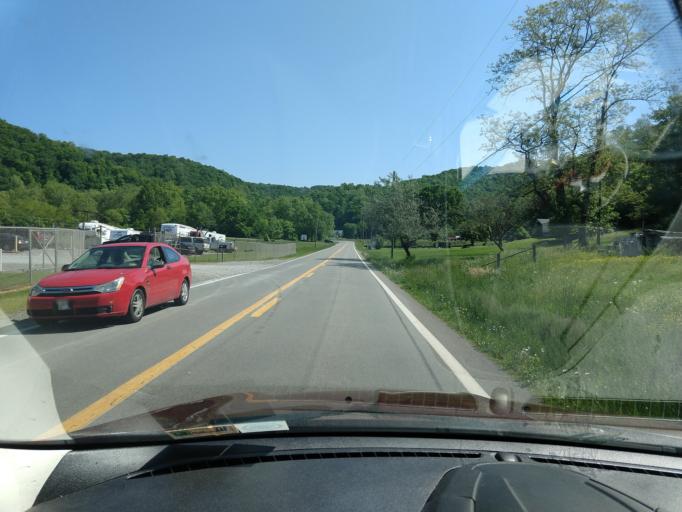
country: US
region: West Virginia
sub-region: Gilmer County
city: Glenville
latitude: 38.8937
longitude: -80.7321
